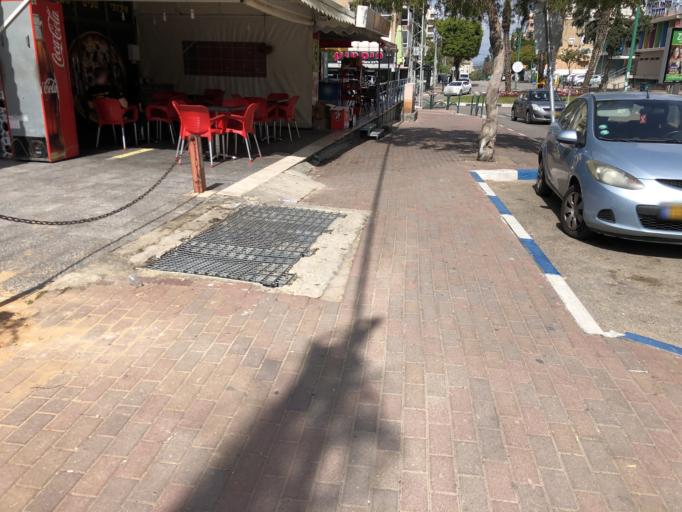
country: IL
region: Haifa
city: Hadera
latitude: 32.4366
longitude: 34.9171
